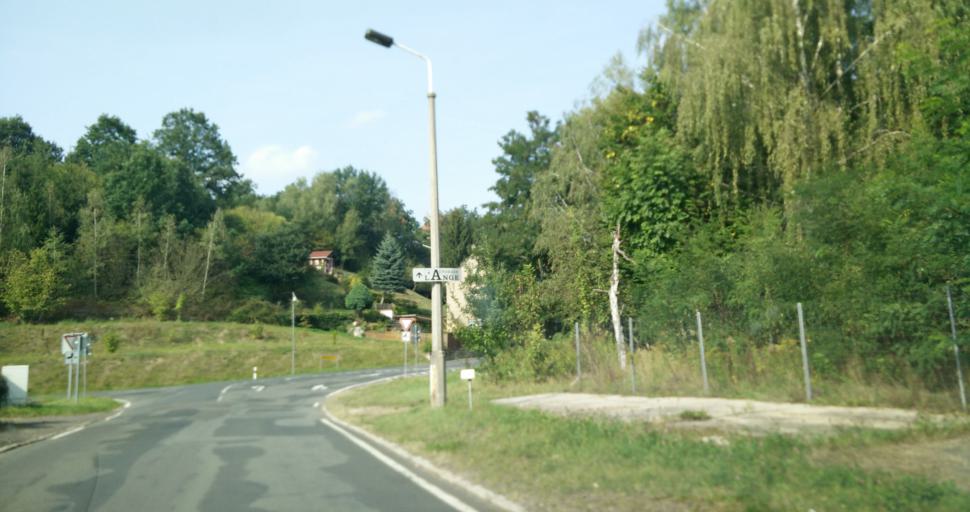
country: DE
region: Saxony
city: Colditz
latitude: 51.1228
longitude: 12.7992
